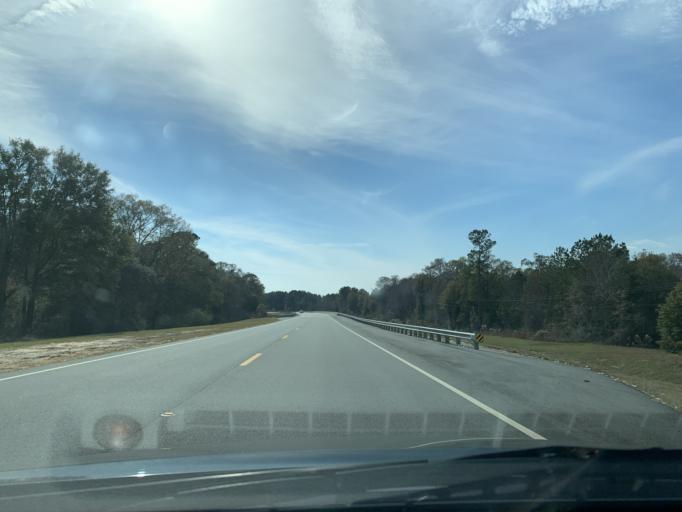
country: US
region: Georgia
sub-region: Turner County
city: Ashburn
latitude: 31.7317
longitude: -83.5785
